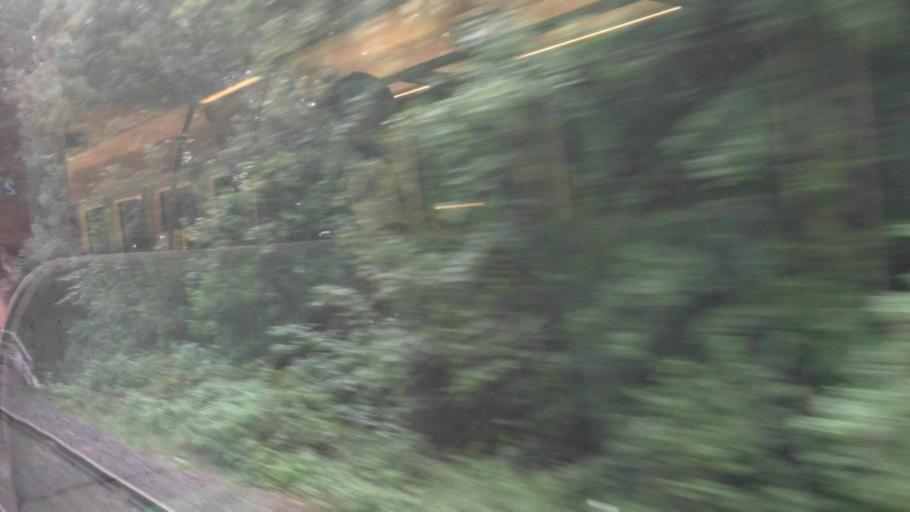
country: DE
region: Saxony
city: Arnsdorf
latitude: 51.1004
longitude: 13.9594
